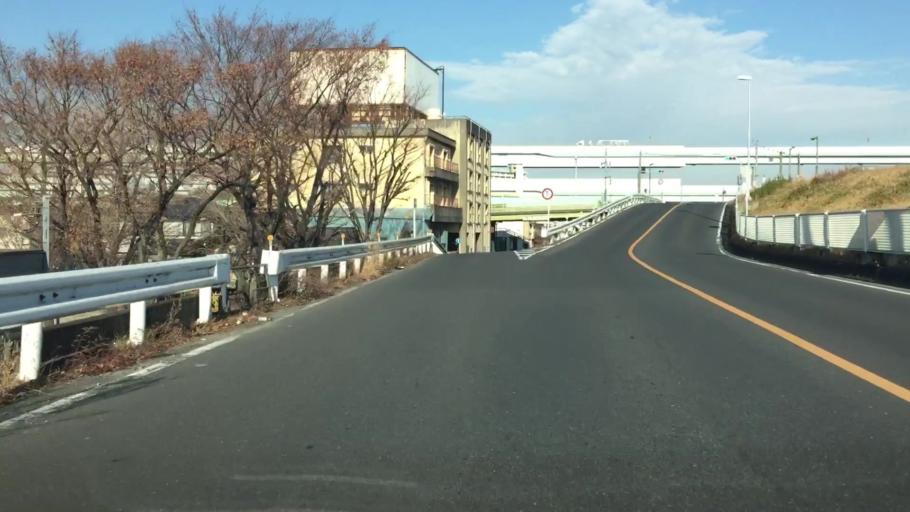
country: JP
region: Saitama
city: Kawaguchi
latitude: 35.7616
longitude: 139.7590
